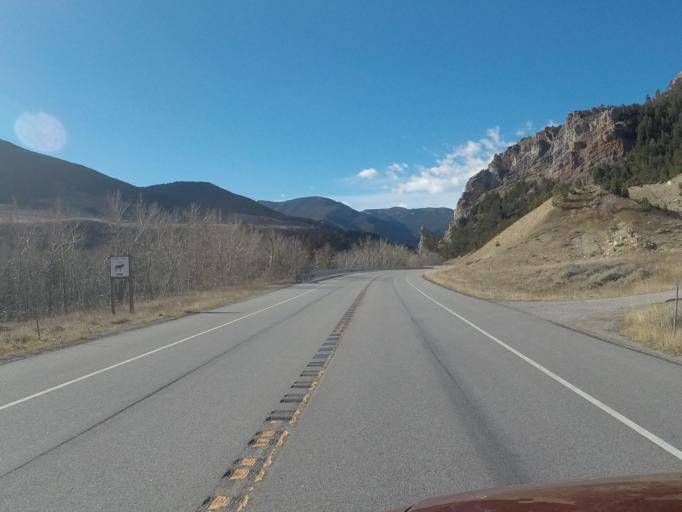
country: US
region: Montana
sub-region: Carbon County
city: Red Lodge
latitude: 45.1378
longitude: -109.2825
